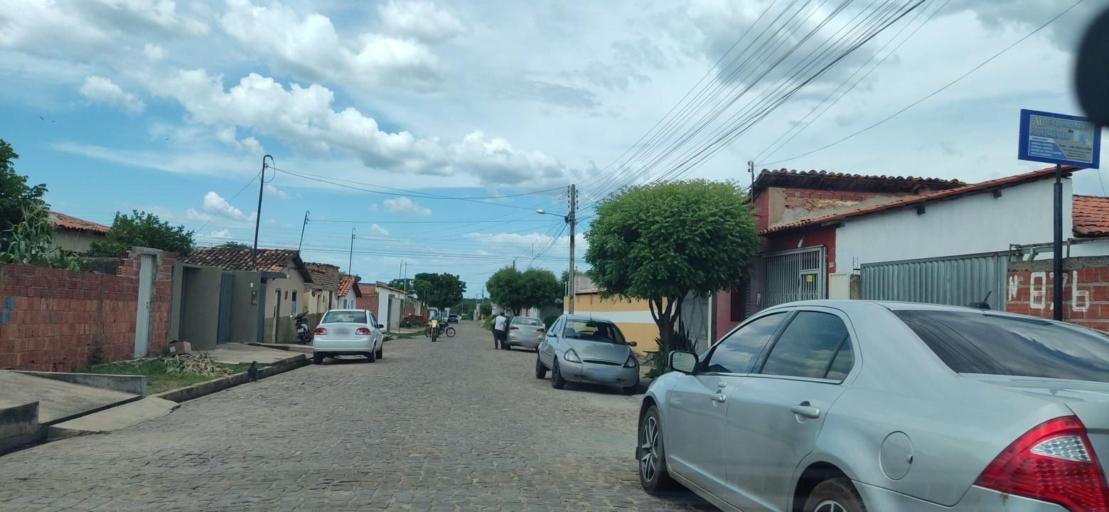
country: BR
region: Piaui
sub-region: Valenca Do Piaui
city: Valenca do Piaui
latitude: -6.4026
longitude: -41.7333
